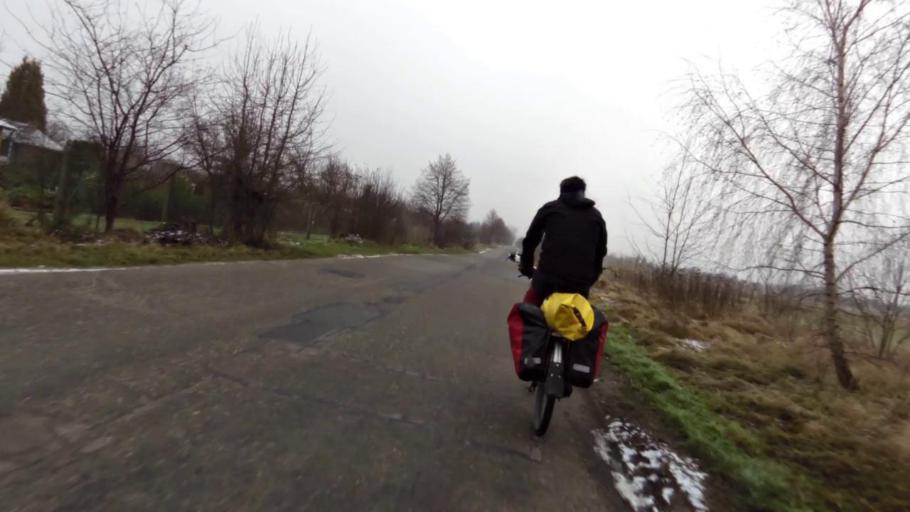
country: PL
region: West Pomeranian Voivodeship
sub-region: Powiat walecki
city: Walcz
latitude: 53.2905
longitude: 16.4750
